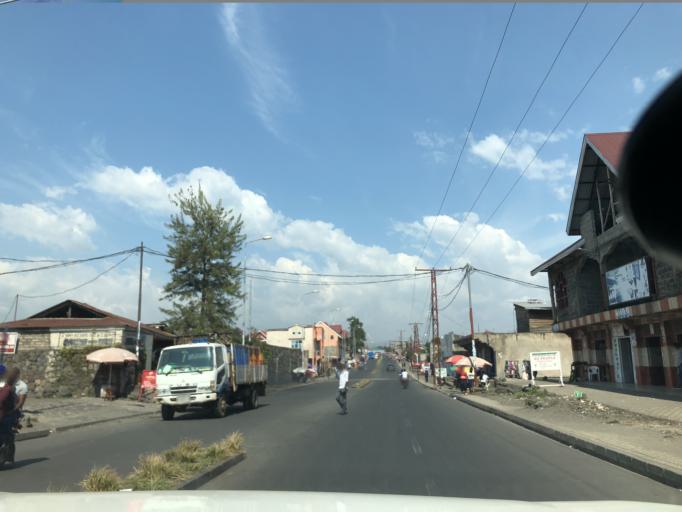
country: CD
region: Nord Kivu
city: Goma
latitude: -1.6580
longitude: 29.1918
